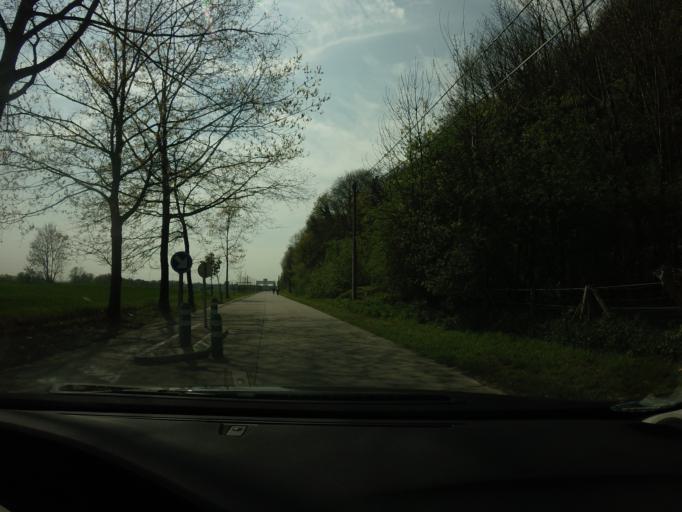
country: NL
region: Limburg
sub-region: Eijsden-Margraten
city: Eijsden
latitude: 50.8026
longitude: 5.6900
